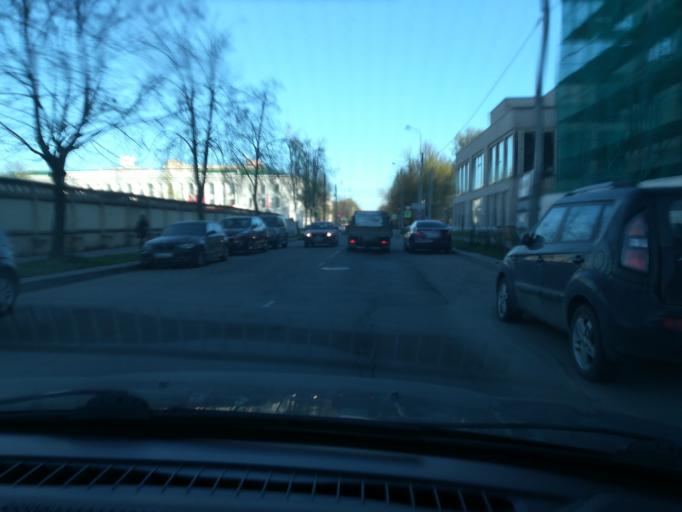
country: RU
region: St.-Petersburg
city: Vasyl'evsky Ostrov
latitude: 59.9373
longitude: 30.2548
